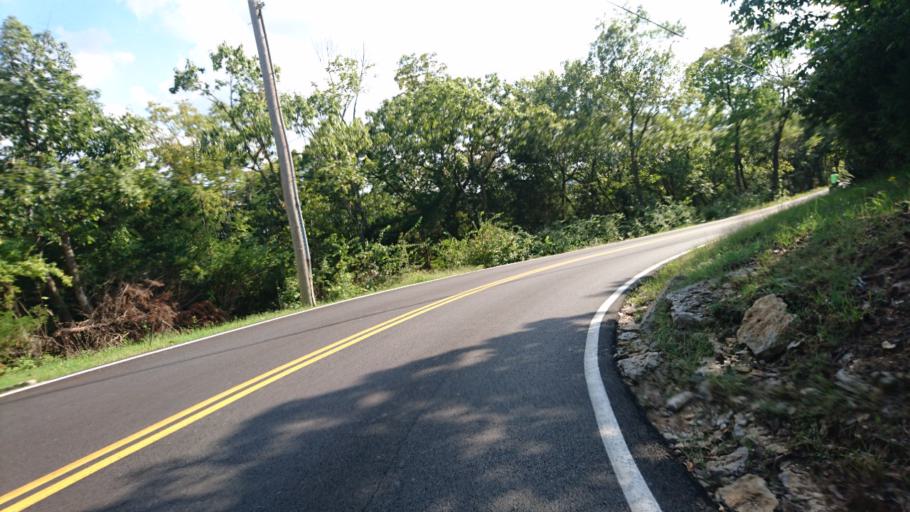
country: US
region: Missouri
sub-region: Saint Louis County
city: Eureka
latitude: 38.5259
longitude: -90.6410
